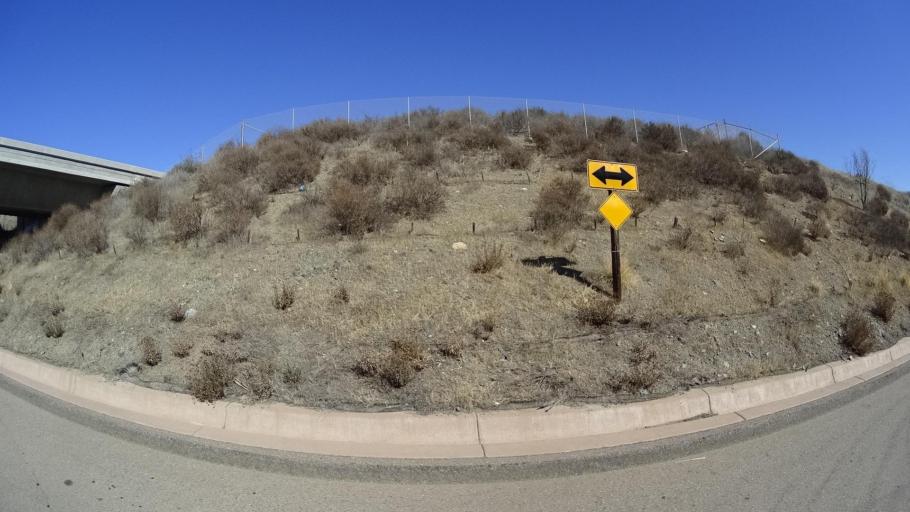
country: US
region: California
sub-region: San Diego County
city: La Presa
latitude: 32.6898
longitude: -117.0165
